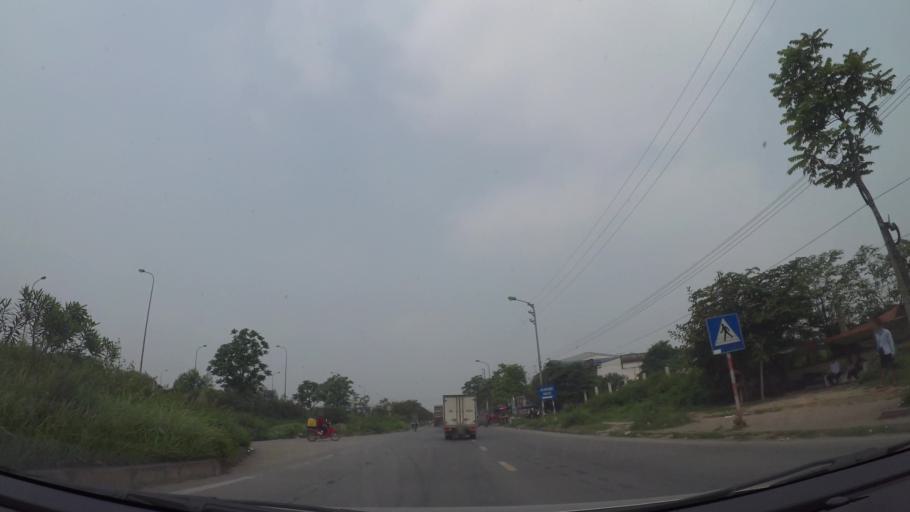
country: VN
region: Ha Noi
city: Quoc Oai
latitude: 21.0036
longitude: 105.6356
